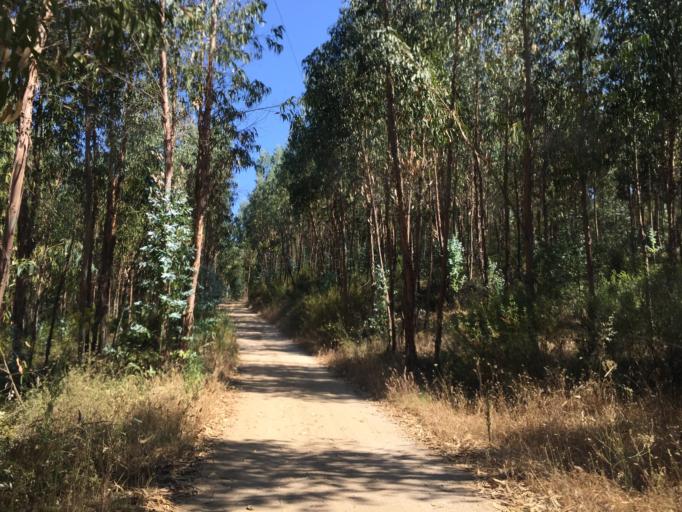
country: PT
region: Santarem
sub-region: Tomar
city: Tomar
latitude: 39.6087
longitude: -8.3491
